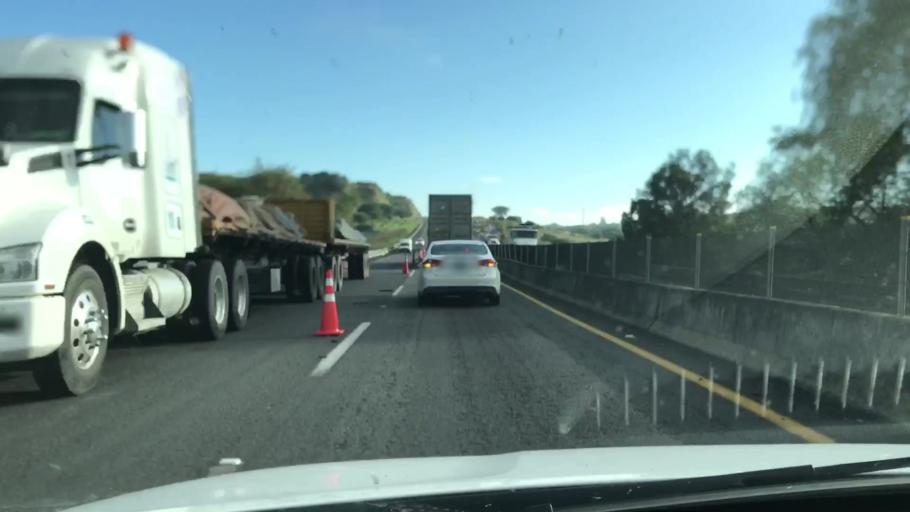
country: MX
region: Jalisco
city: Jalostotitlan
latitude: 21.1068
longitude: -102.4691
